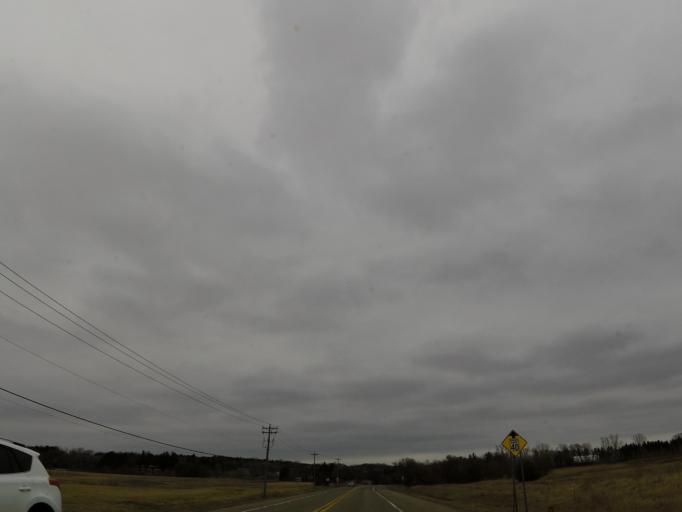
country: US
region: Minnesota
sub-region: Washington County
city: Bayport
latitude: 45.0138
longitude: -92.7965
